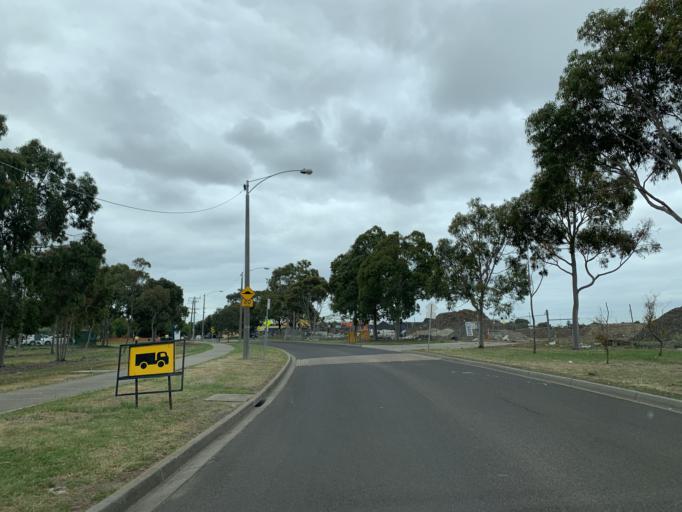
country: AU
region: Victoria
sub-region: Brimbank
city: St Albans
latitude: -37.7490
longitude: 144.7990
